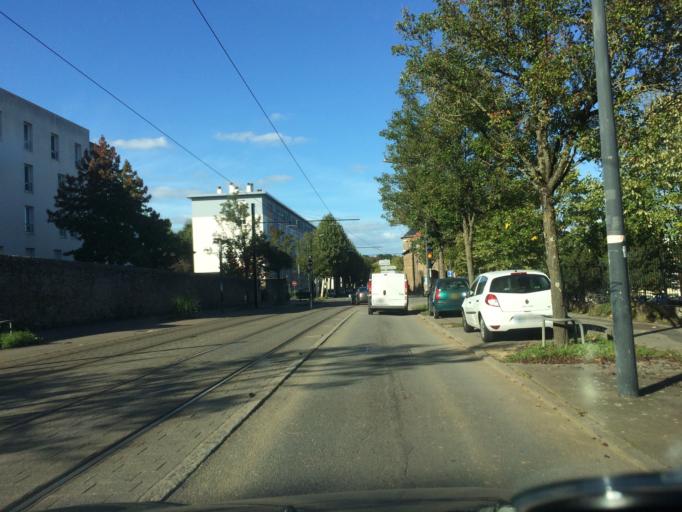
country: FR
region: Pays de la Loire
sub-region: Departement de la Loire-Atlantique
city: Nantes
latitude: 47.2376
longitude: -1.5566
